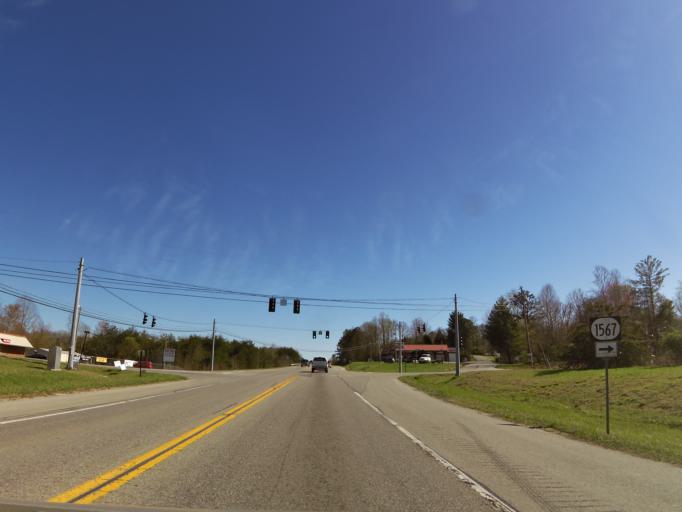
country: US
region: Kentucky
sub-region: McCreary County
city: Stearns
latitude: 36.6945
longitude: -84.4562
